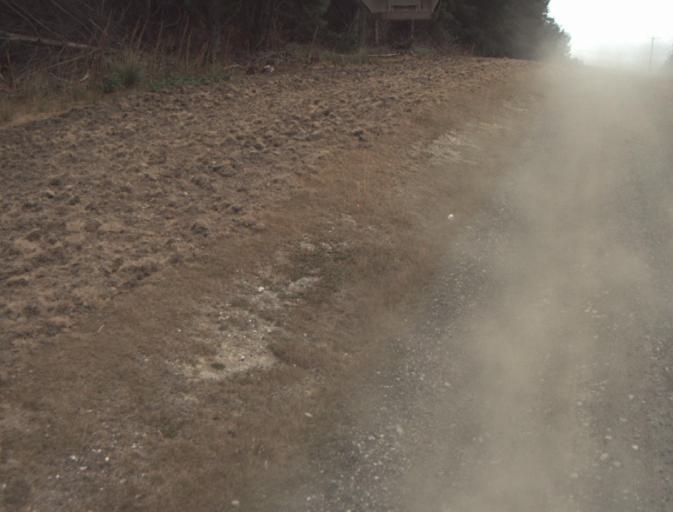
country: AU
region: Tasmania
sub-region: Launceston
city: Mayfield
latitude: -41.1524
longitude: 147.1745
